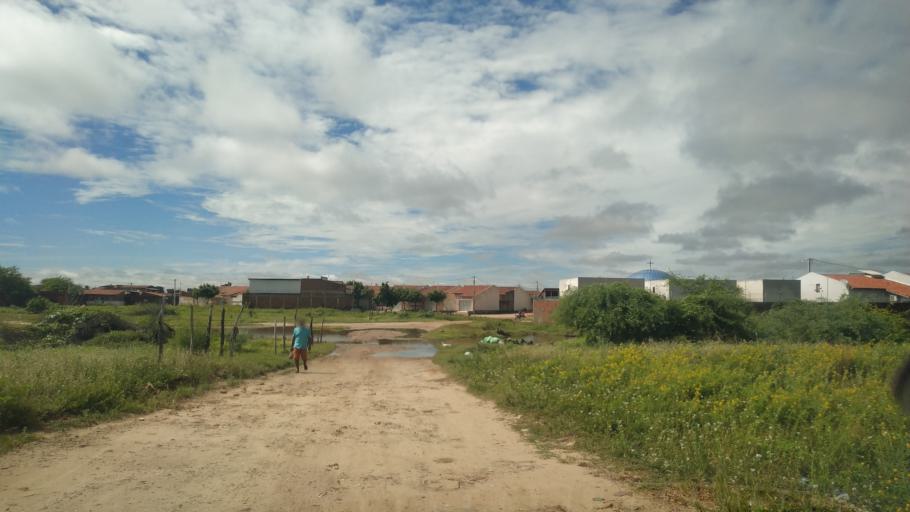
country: BR
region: Rio Grande do Norte
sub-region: Areia Branca
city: Areia Branca
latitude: -4.9515
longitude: -37.1233
